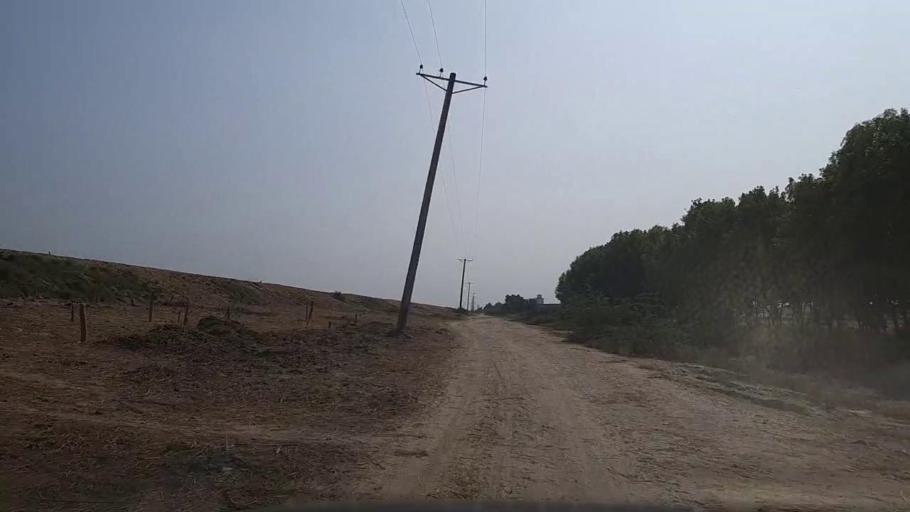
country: PK
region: Sindh
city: Chuhar Jamali
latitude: 24.5600
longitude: 67.9145
